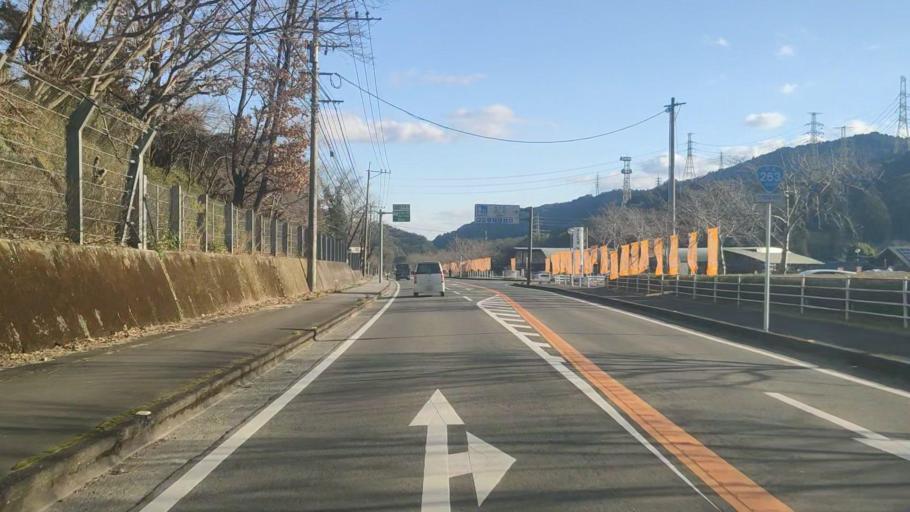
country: JP
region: Saga Prefecture
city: Saga-shi
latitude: 33.3404
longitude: 130.2573
